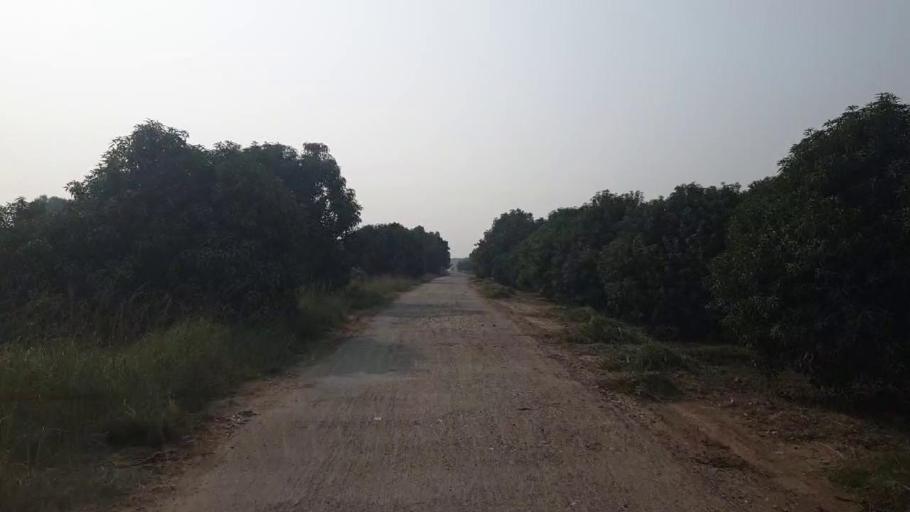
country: PK
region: Sindh
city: Tando Jam
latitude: 25.3303
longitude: 68.5180
